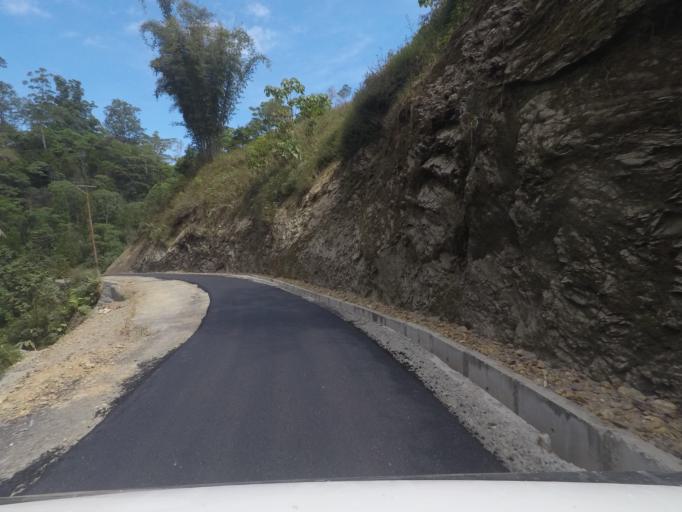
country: TL
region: Ermera
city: Gleno
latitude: -8.7532
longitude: 125.3372
